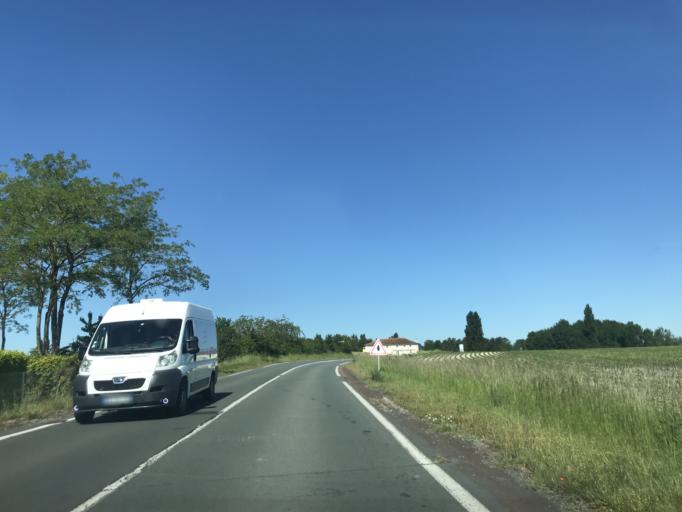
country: FR
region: Poitou-Charentes
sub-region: Departement de la Charente
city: Barbezieux-Saint-Hilaire
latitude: 45.4984
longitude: -0.2476
